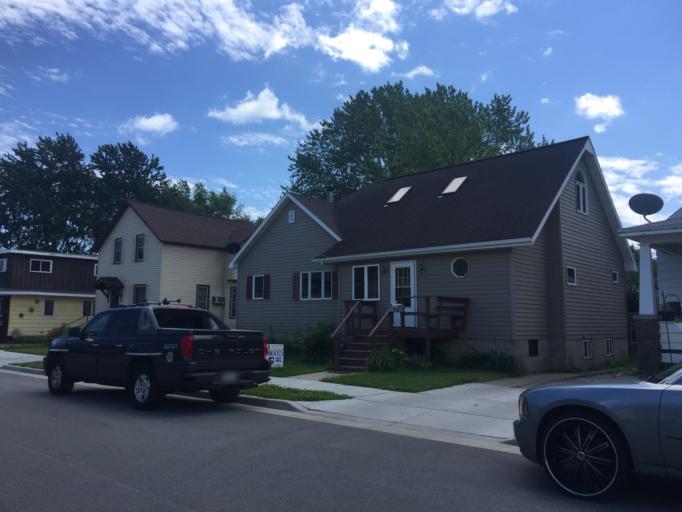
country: US
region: Wisconsin
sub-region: Marinette County
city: Marinette
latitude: 45.0892
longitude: -87.6205
